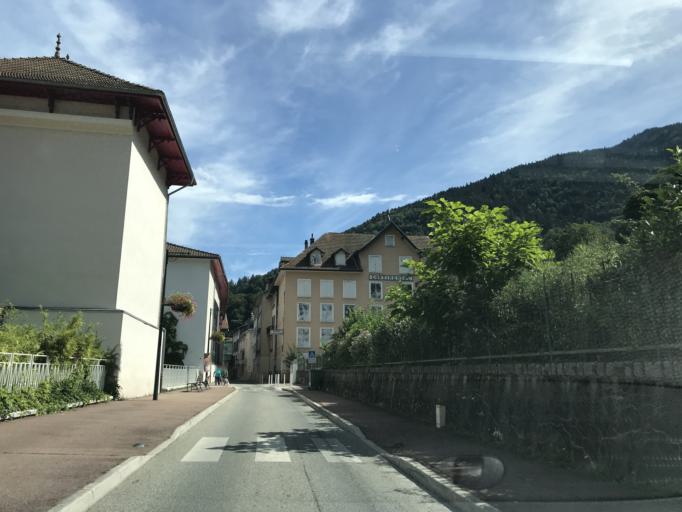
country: FR
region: Rhone-Alpes
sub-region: Departement de l'Isere
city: Allevard
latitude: 45.3910
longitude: 6.0738
